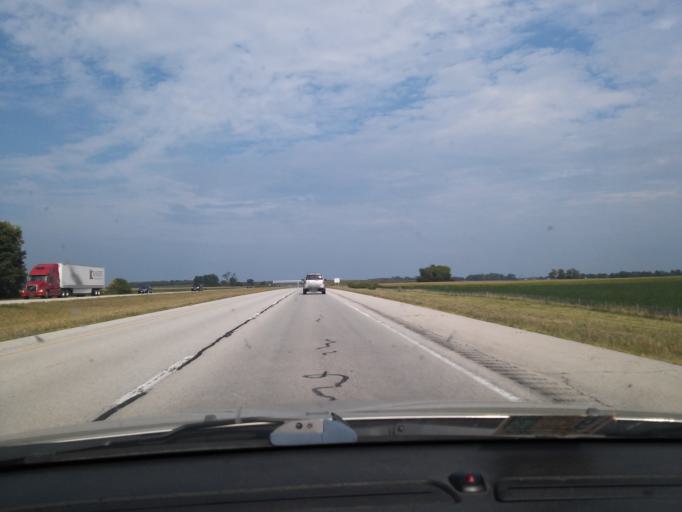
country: US
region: Ohio
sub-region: Greene County
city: Jamestown
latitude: 39.6484
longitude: -83.6742
